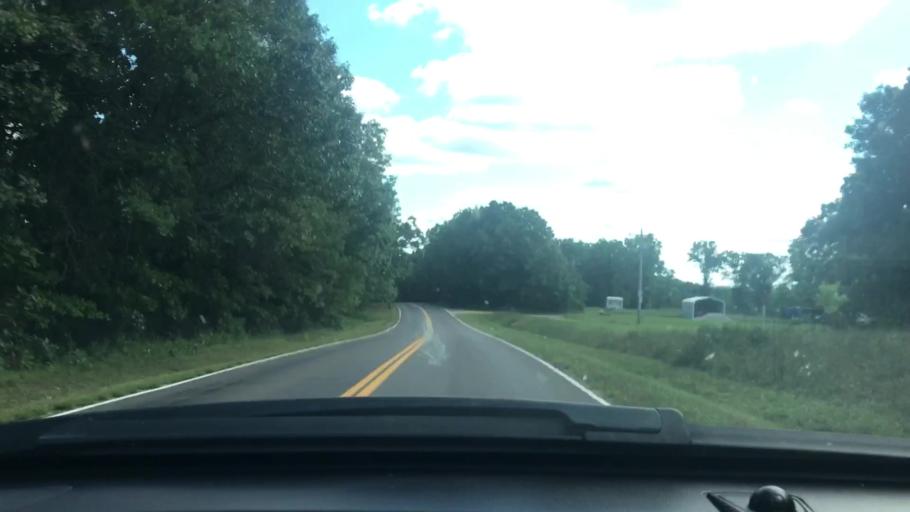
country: US
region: Missouri
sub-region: Wright County
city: Hartville
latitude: 37.3563
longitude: -92.3417
